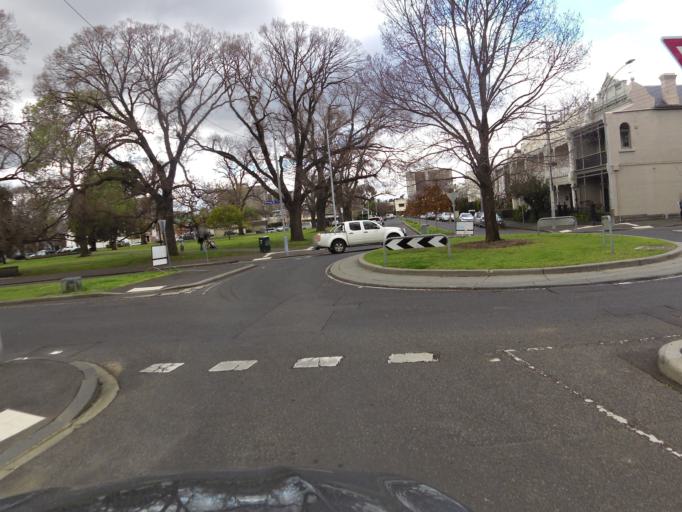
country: AU
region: Victoria
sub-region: Melbourne
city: East Melbourne
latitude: -37.8133
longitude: 144.9881
